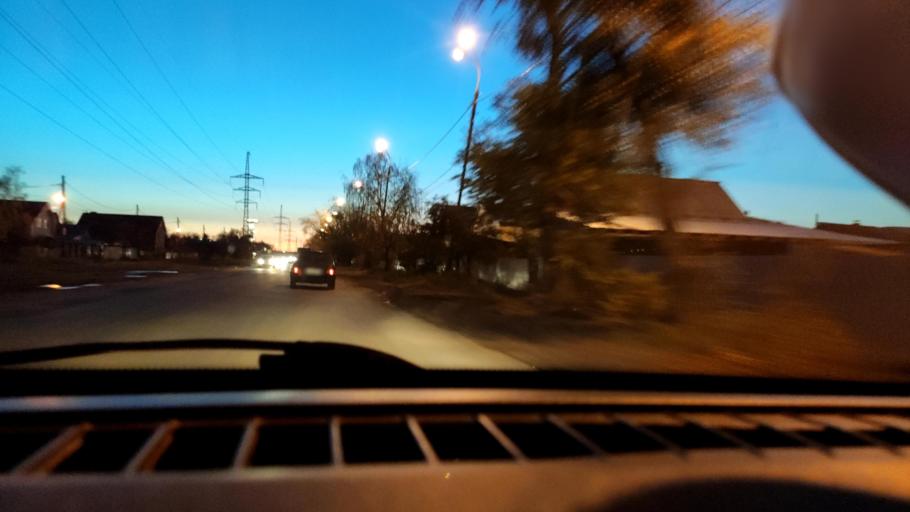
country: RU
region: Samara
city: Samara
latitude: 53.1336
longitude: 50.1293
